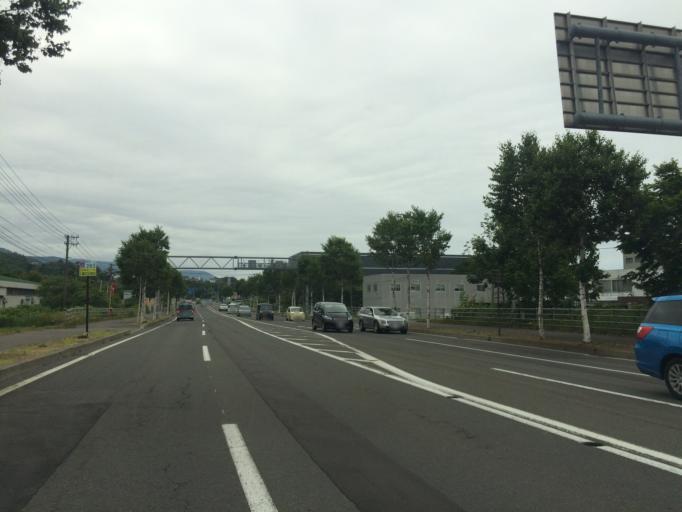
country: JP
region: Hokkaido
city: Sapporo
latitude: 43.1316
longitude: 141.1915
